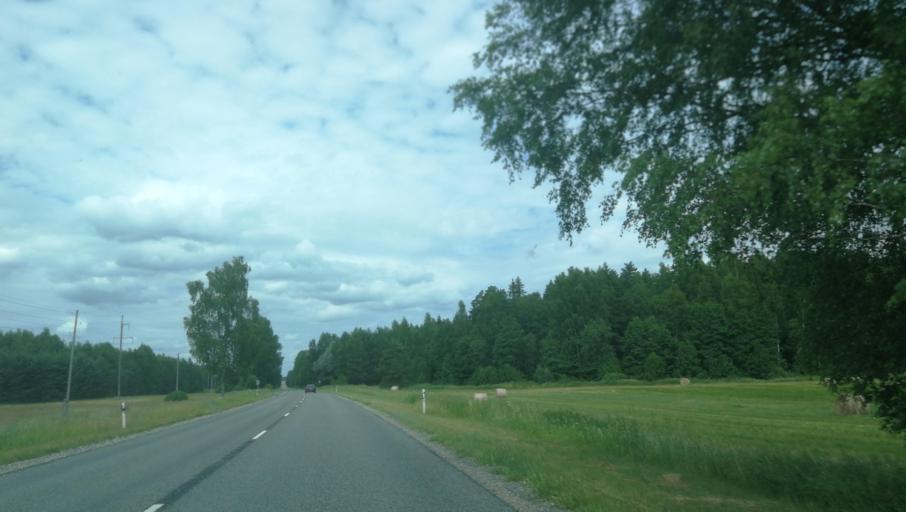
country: LV
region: Naukseni
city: Naukseni
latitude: 57.7759
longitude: 25.4310
